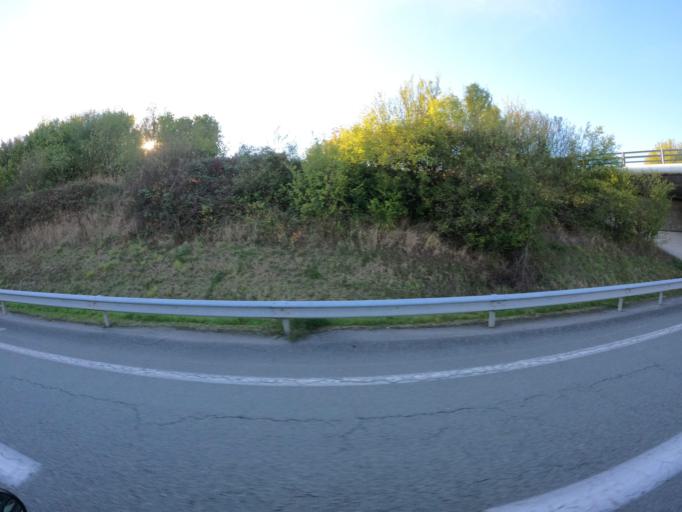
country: FR
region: Pays de la Loire
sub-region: Departement de Maine-et-Loire
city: Nuaille
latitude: 47.0827
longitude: -0.8248
